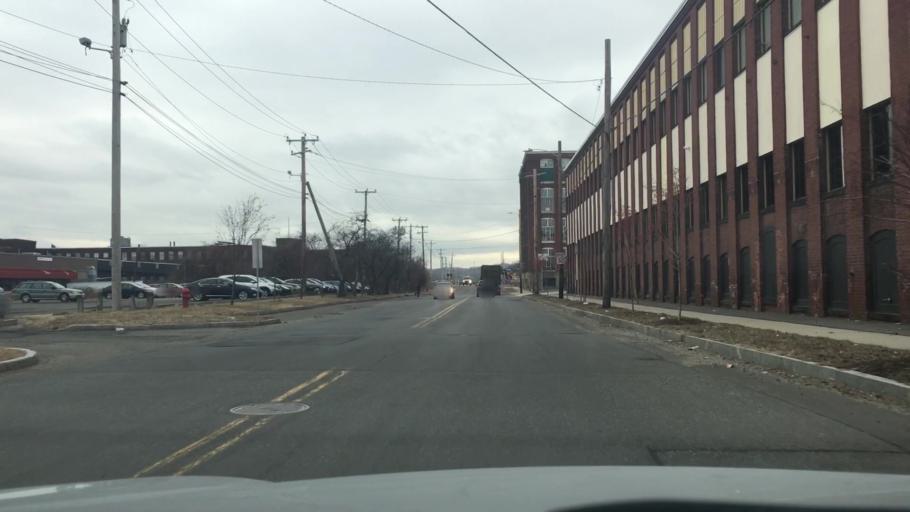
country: US
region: Massachusetts
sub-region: Hampden County
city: North Chicopee
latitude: 42.1991
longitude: -72.6005
